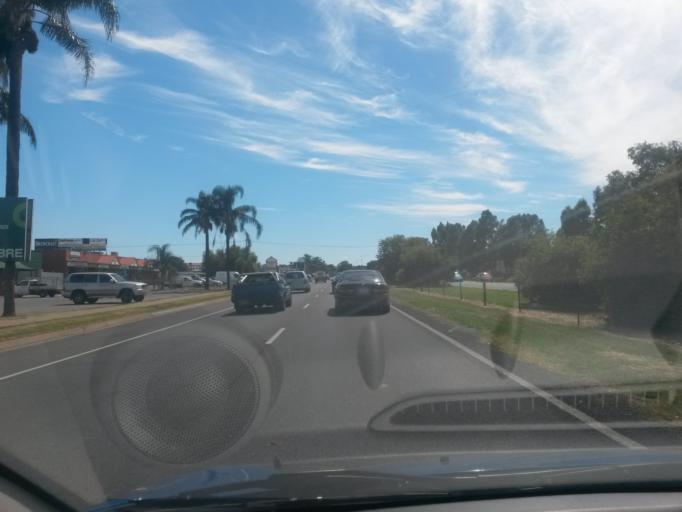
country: AU
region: South Australia
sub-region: Salisbury
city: Salisbury
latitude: -34.7735
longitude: 138.6630
